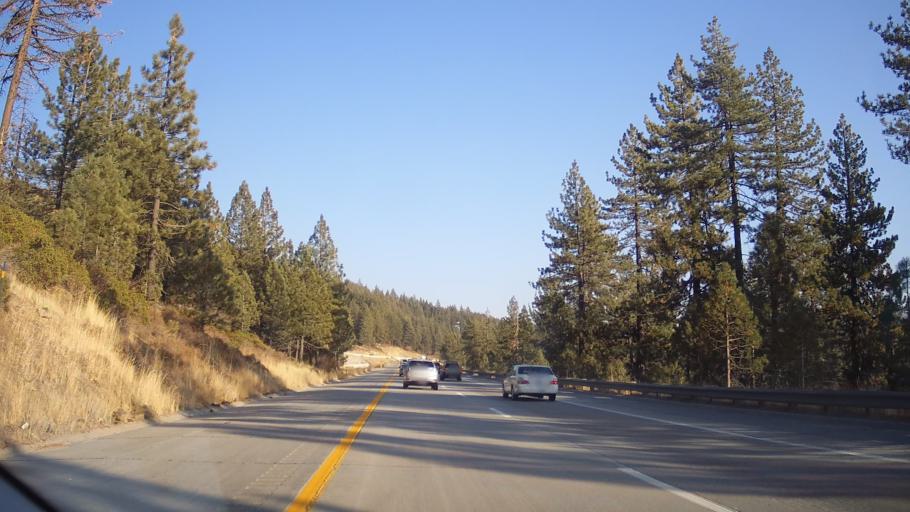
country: US
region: California
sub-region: Nevada County
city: Truckee
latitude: 39.3313
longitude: -120.2521
